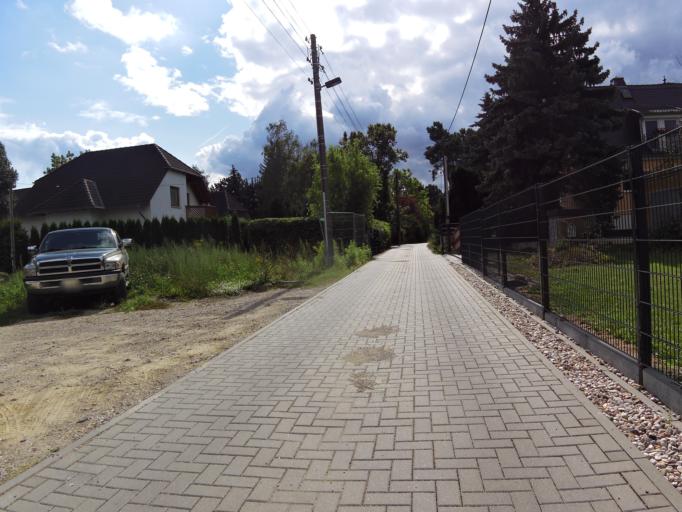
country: DE
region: Saxony
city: Rackwitz
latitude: 51.3903
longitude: 12.3604
